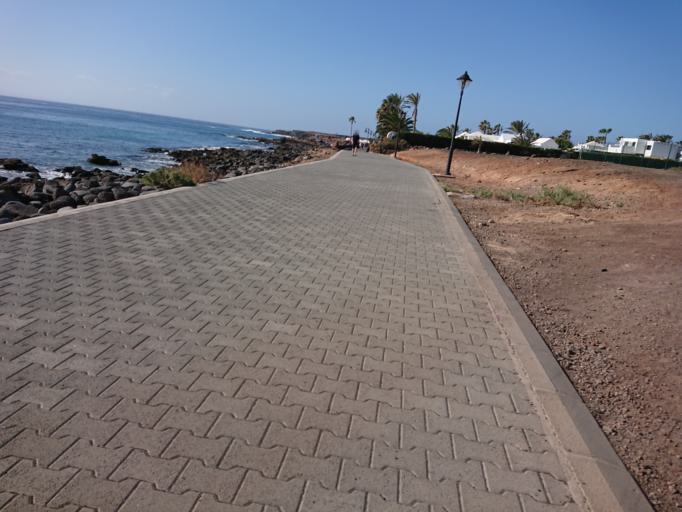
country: ES
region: Canary Islands
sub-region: Provincia de Las Palmas
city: Playa Blanca
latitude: 28.8607
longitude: -13.8634
